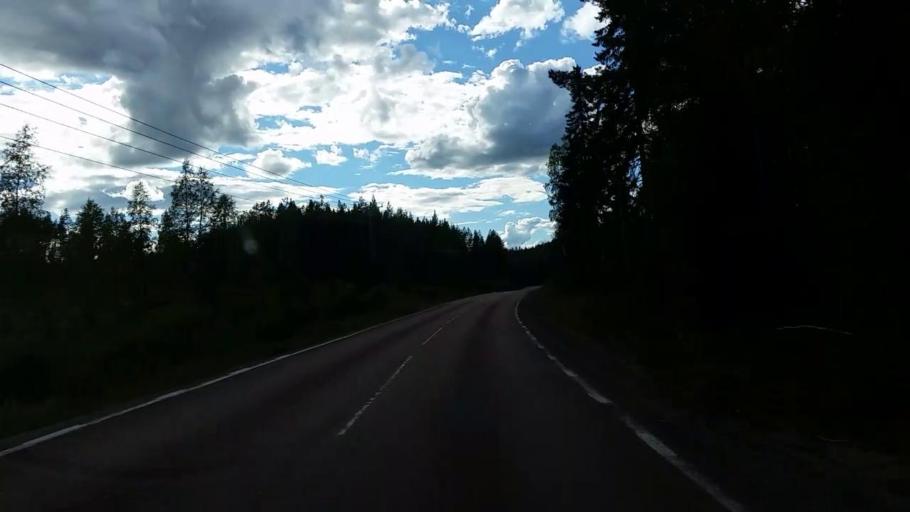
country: SE
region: Gaevleborg
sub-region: Ljusdals Kommun
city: Farila
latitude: 62.0117
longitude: 15.9017
